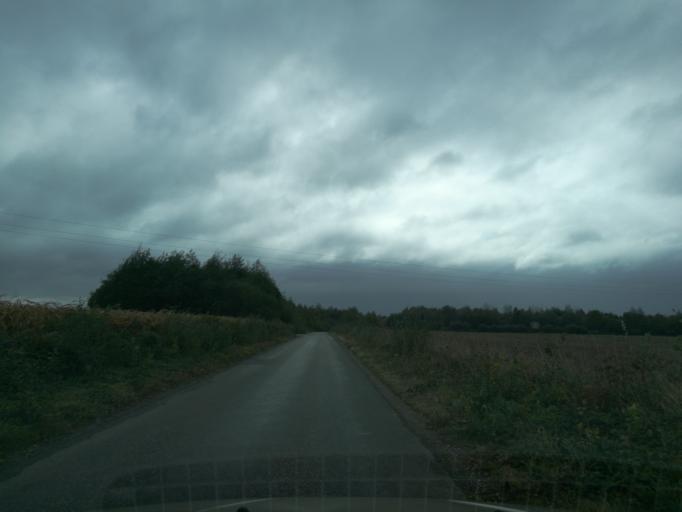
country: FR
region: Brittany
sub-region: Departement d'Ille-et-Vilaine
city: Pleumeleuc
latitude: 48.1729
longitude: -1.8993
